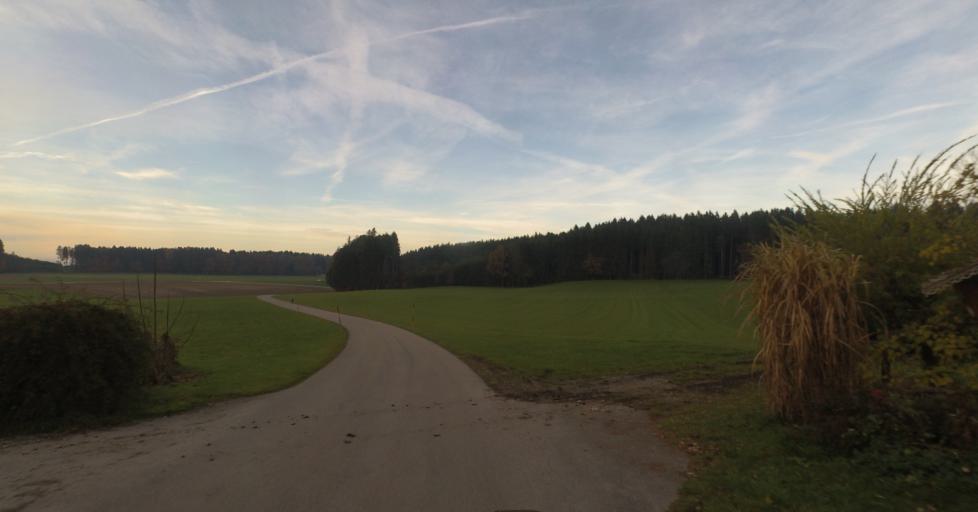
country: DE
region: Bavaria
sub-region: Upper Bavaria
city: Nussdorf
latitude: 47.8940
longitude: 12.5962
